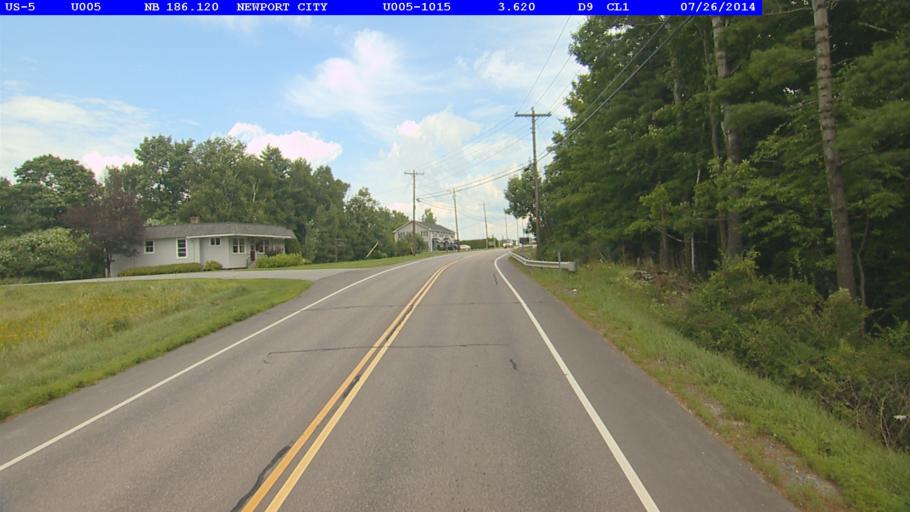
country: US
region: Vermont
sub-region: Orleans County
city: Newport
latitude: 44.9470
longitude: -72.1745
